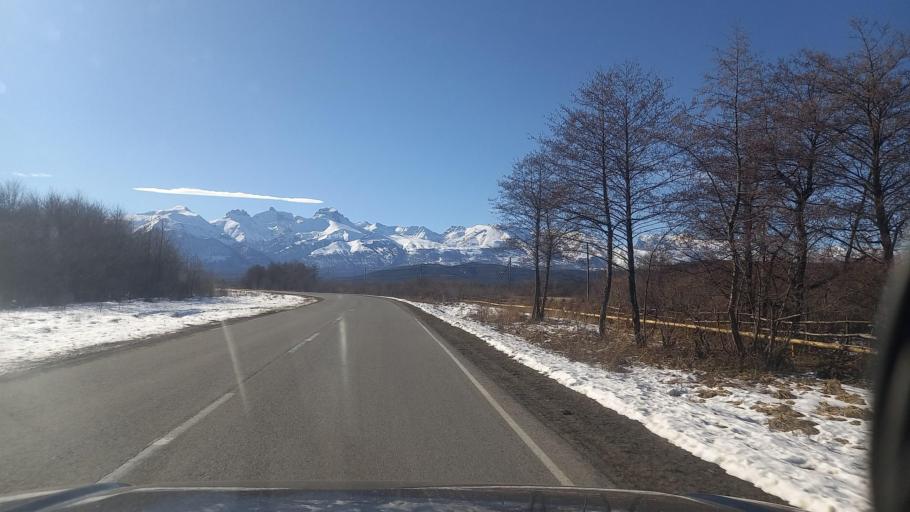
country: RU
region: North Ossetia
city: Chikola
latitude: 43.1531
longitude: 43.8403
